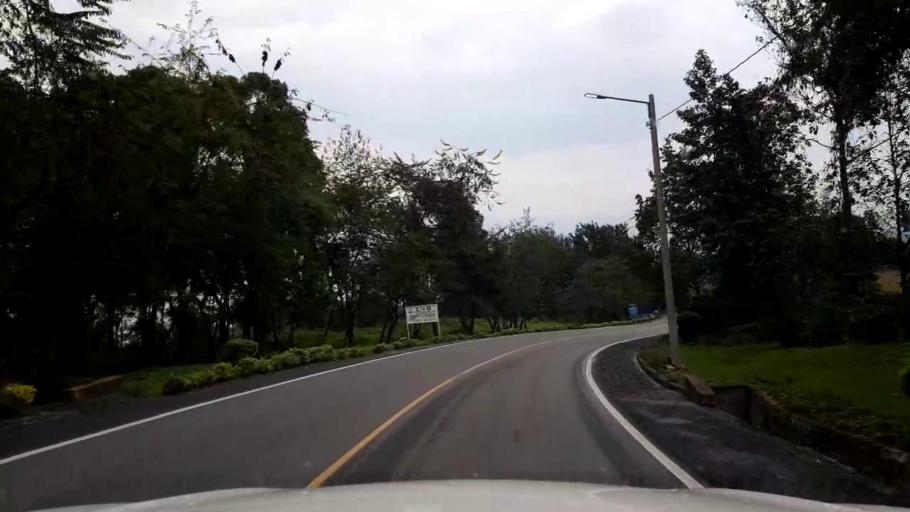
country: RW
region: Western Province
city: Gisenyi
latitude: -1.7045
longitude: 29.2667
